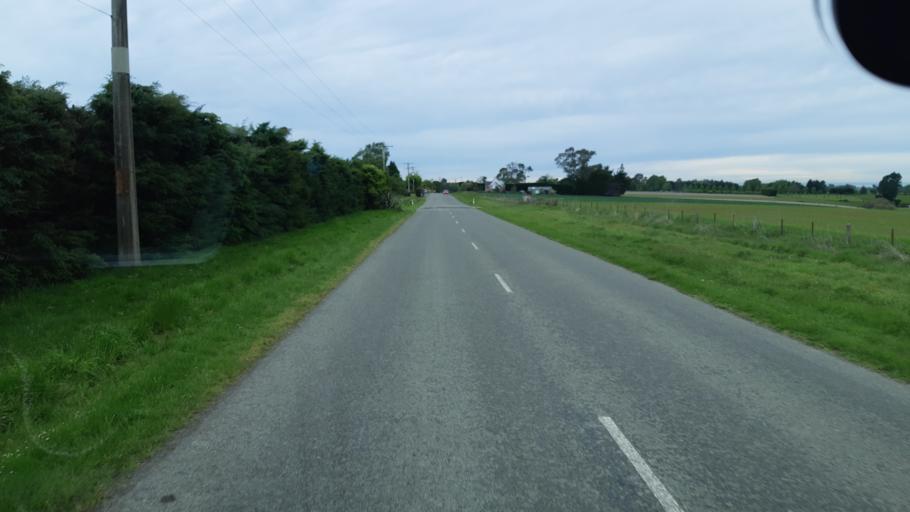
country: NZ
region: Canterbury
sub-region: Timaru District
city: Timaru
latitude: -44.4106
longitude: 171.1774
